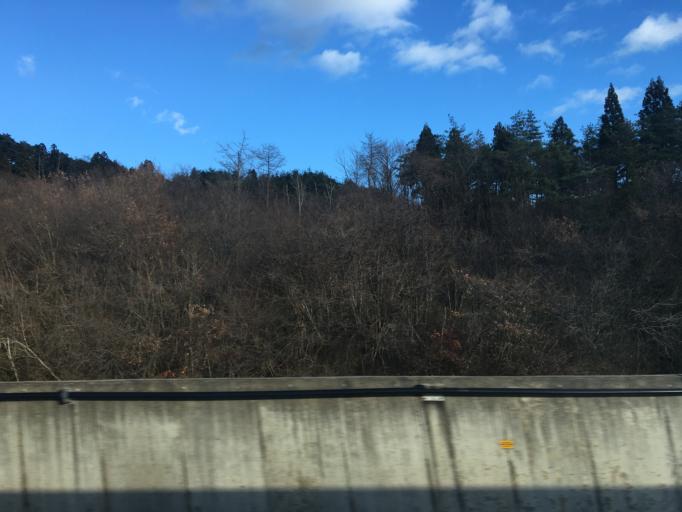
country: JP
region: Iwate
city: Mizusawa
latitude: 39.1236
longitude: 141.1939
